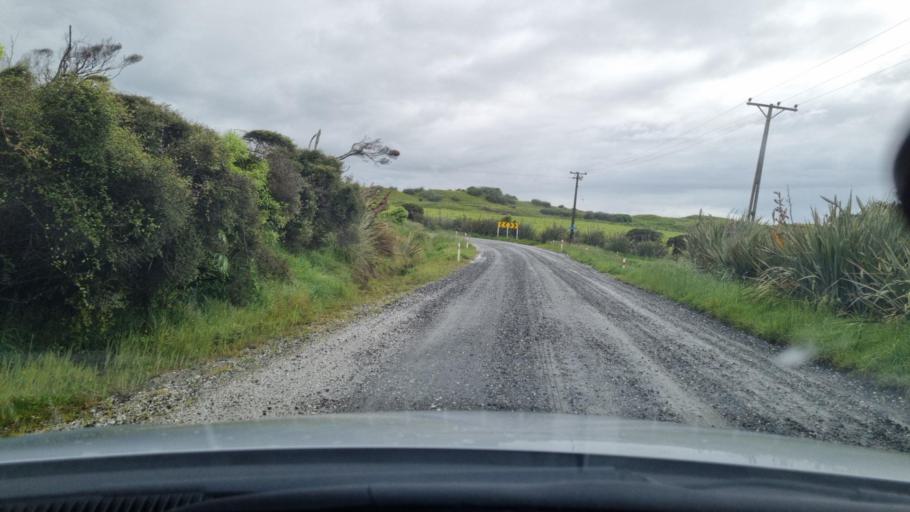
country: NZ
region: Southland
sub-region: Invercargill City
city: Bluff
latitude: -46.5209
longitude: 168.2723
